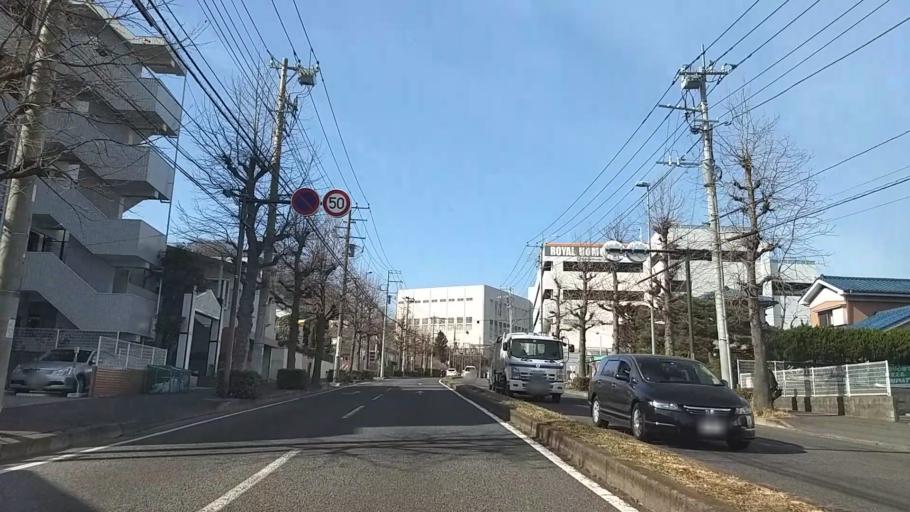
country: JP
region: Kanagawa
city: Kamakura
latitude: 35.3670
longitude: 139.5886
